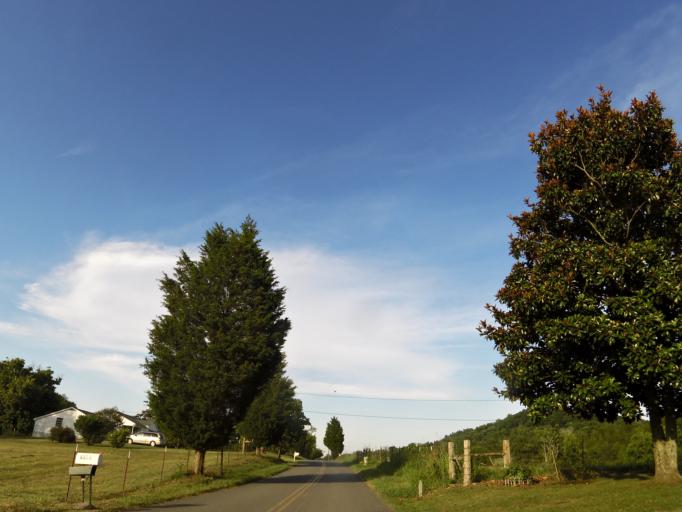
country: US
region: Tennessee
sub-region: Blount County
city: Eagleton Village
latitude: 35.8587
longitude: -83.9173
